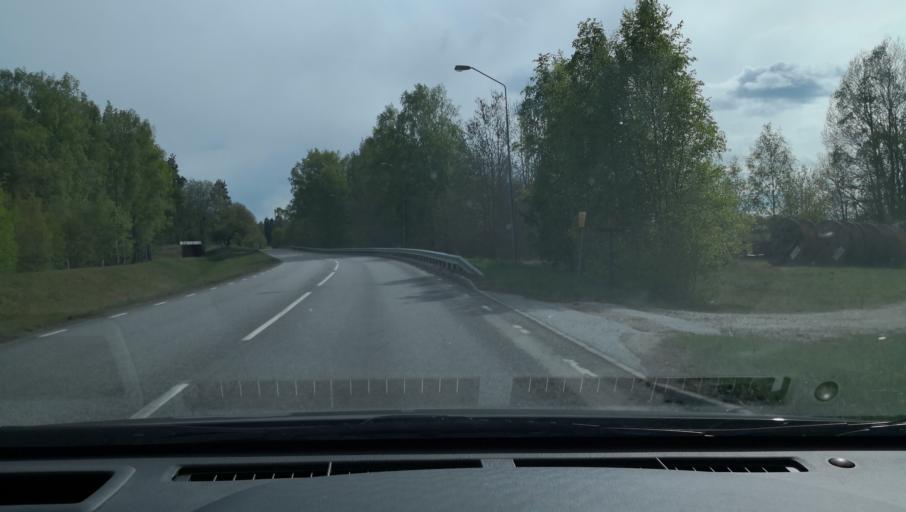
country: SE
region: OErebro
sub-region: Kumla Kommun
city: Kumla
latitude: 59.1051
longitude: 15.1639
